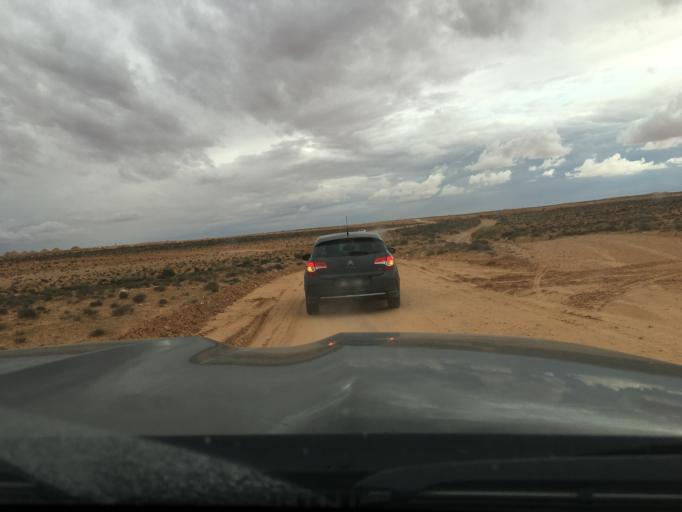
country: TN
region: Madanin
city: Medenine
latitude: 33.2621
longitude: 10.5721
